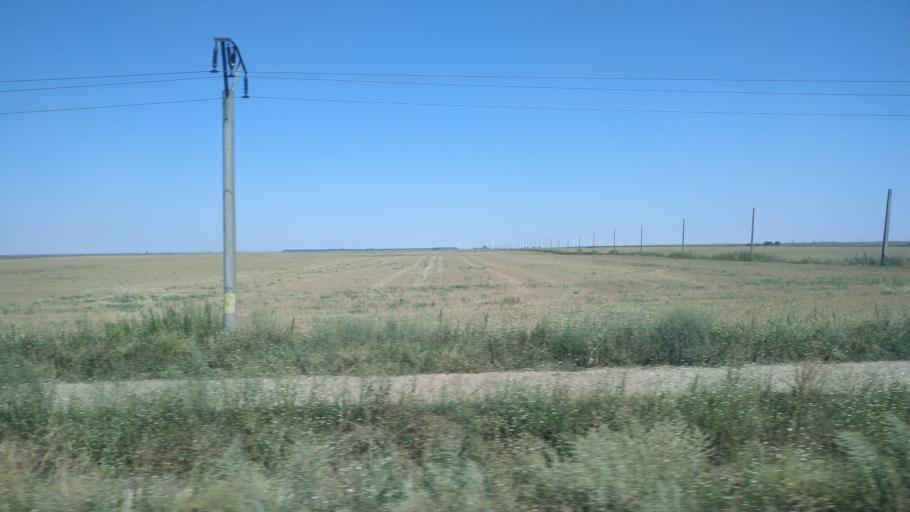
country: RO
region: Ialomita
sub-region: Municipiul Fetesti
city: Buliga
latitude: 44.4194
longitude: 27.7298
